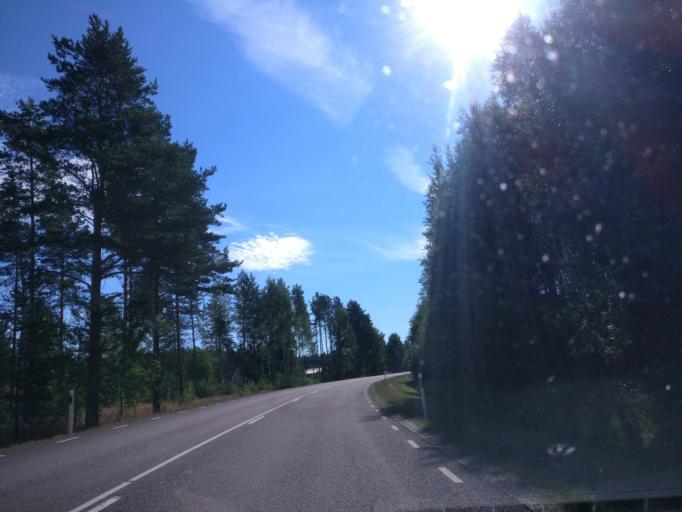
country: SE
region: Vaermland
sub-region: Hagfors Kommun
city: Hagfors
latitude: 60.0669
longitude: 13.7285
